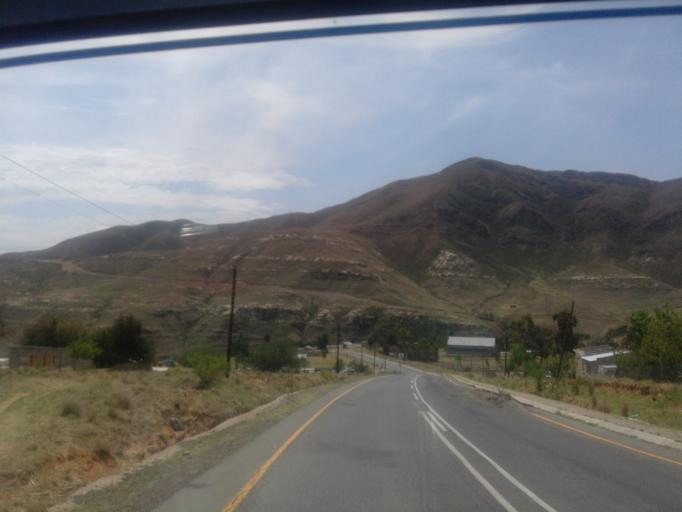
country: LS
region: Qacha's Nek
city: Qacha's Nek
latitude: -30.1069
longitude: 28.6704
